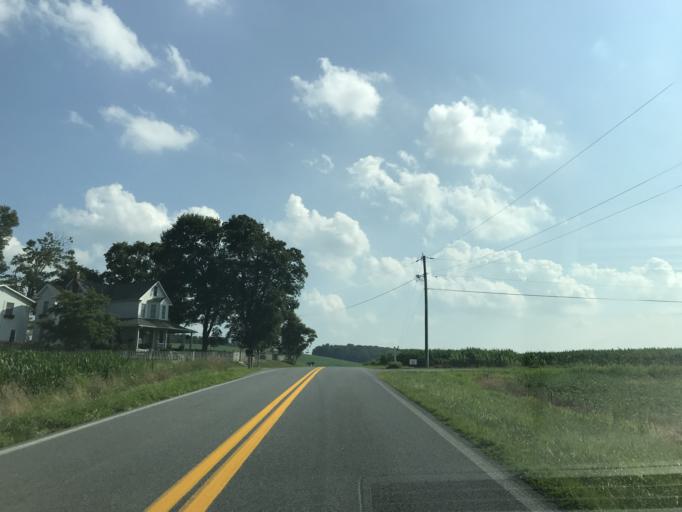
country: US
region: Maryland
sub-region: Carroll County
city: Manchester
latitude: 39.6449
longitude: -76.9382
